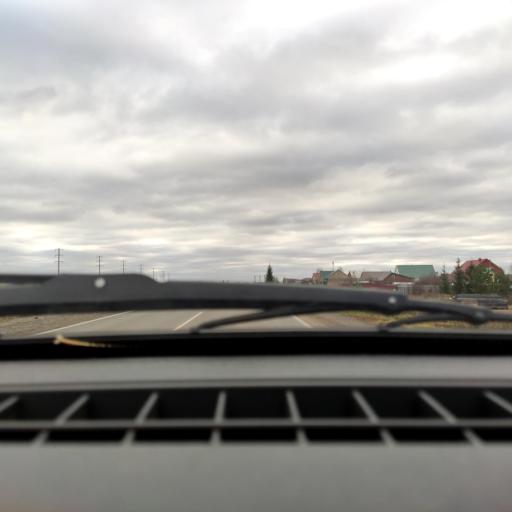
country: RU
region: Bashkortostan
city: Iglino
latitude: 54.7838
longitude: 56.2527
